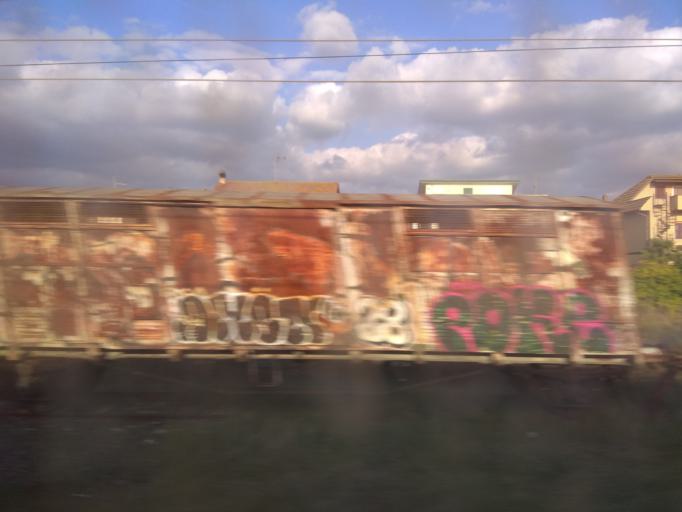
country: IT
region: Latium
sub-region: Citta metropolitana di Roma Capitale
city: Maccarese
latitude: 41.8737
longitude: 12.2426
